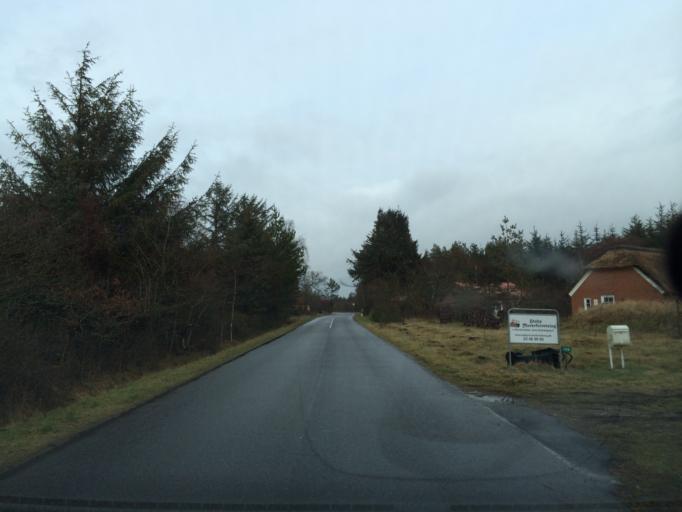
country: DK
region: Central Jutland
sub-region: Holstebro Kommune
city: Ulfborg
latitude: 56.2609
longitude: 8.1487
